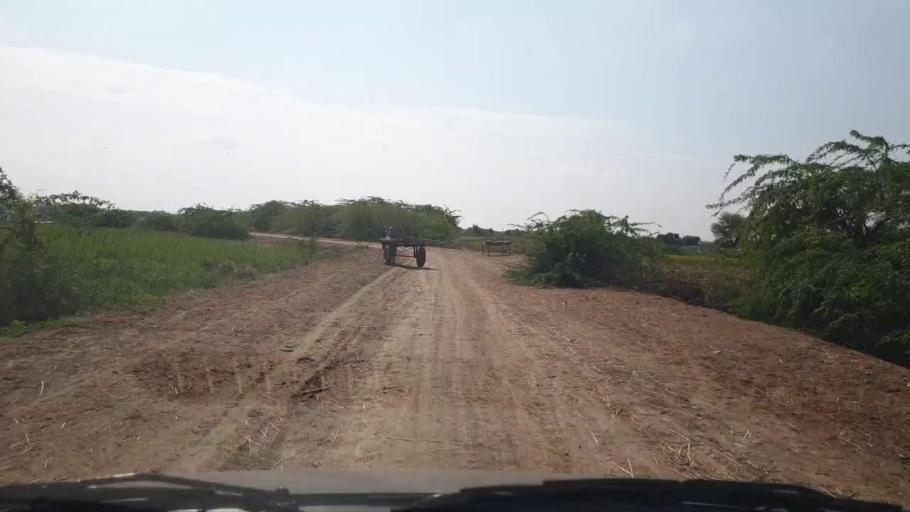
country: PK
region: Sindh
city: Badin
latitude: 24.4843
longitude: 68.6118
